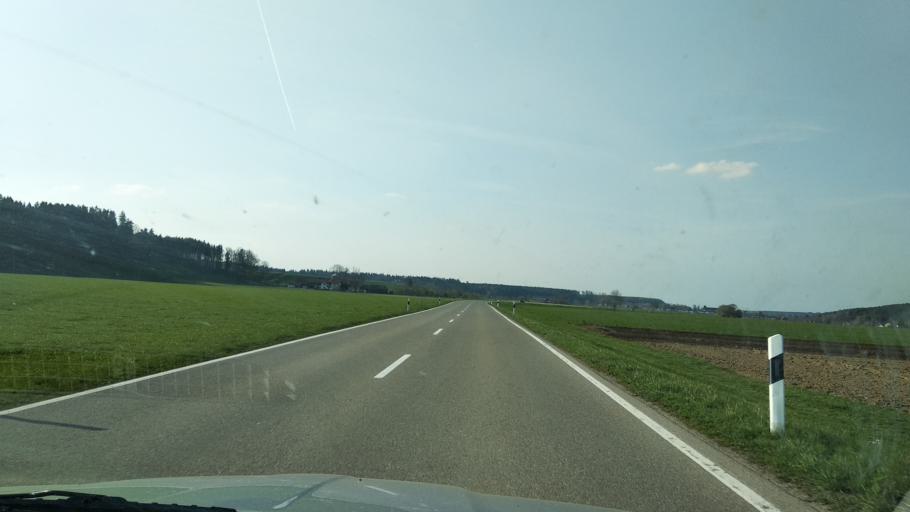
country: DE
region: Bavaria
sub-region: Swabia
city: Legau
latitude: 47.8747
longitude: 10.1232
